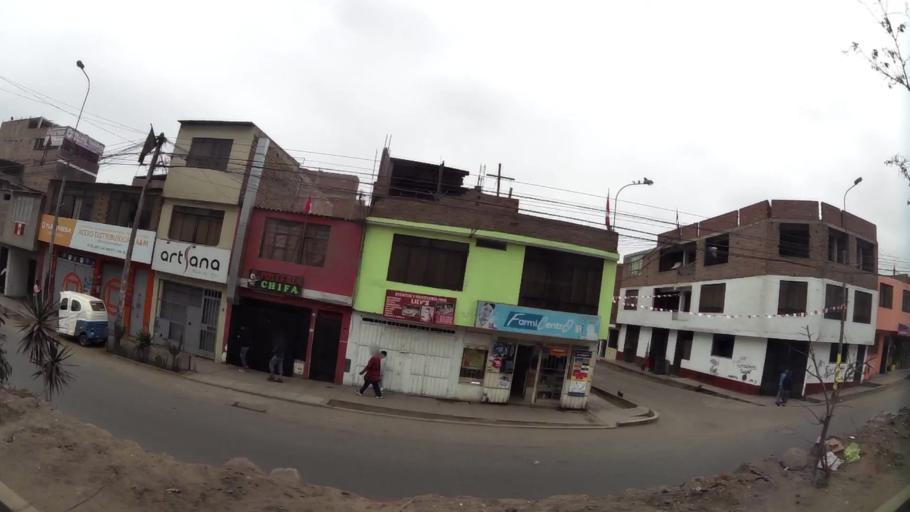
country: PE
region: Lima
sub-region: Lima
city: Surco
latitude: -12.1459
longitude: -76.9701
